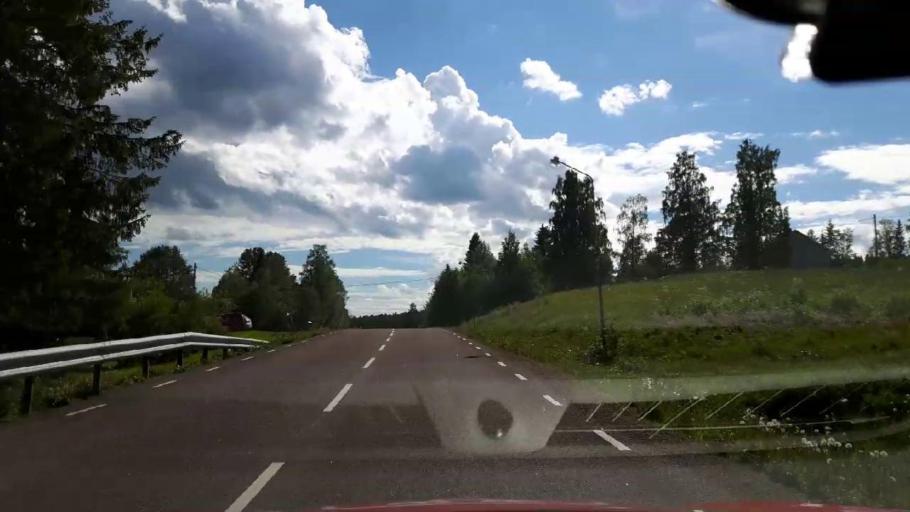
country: SE
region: Jaemtland
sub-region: Krokoms Kommun
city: Valla
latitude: 63.9864
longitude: 14.2260
